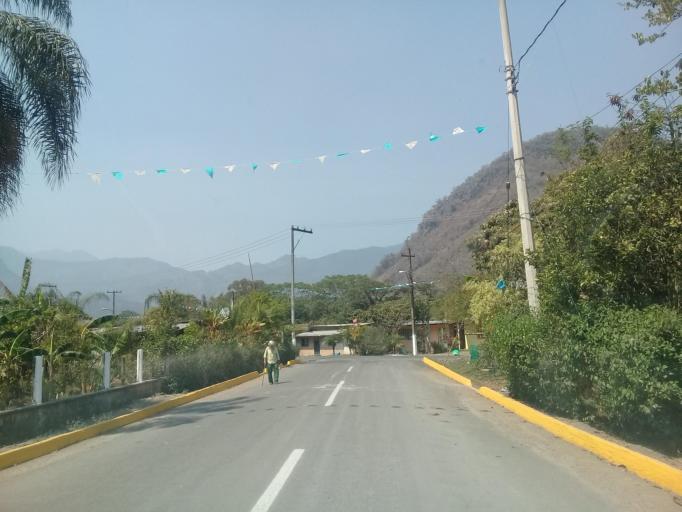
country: MX
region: Veracruz
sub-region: Ixtaczoquitlan
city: Capoluca
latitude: 18.8042
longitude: -96.9910
